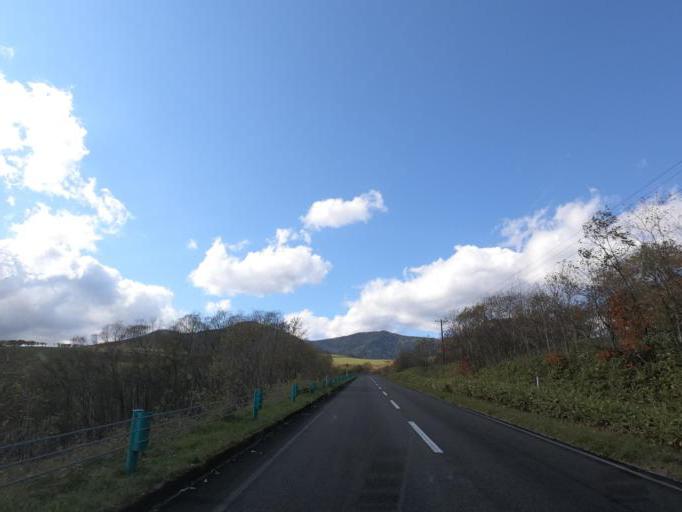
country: JP
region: Hokkaido
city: Otofuke
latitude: 43.2915
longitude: 143.2026
